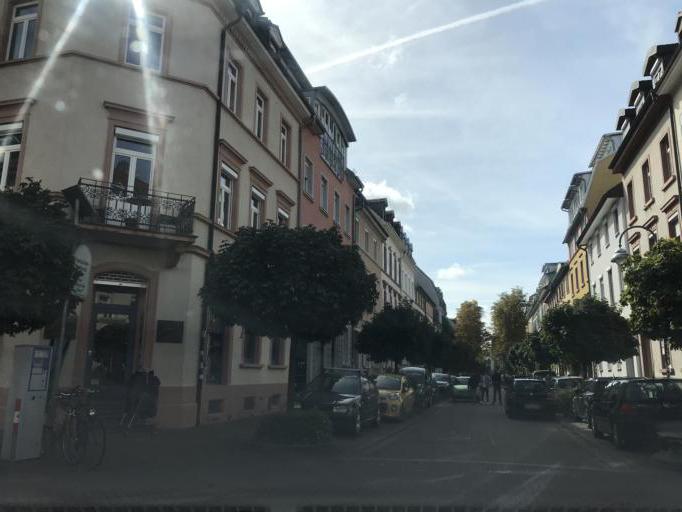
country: DE
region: Baden-Wuerttemberg
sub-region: Freiburg Region
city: Freiburg
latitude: 47.9990
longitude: 7.8400
